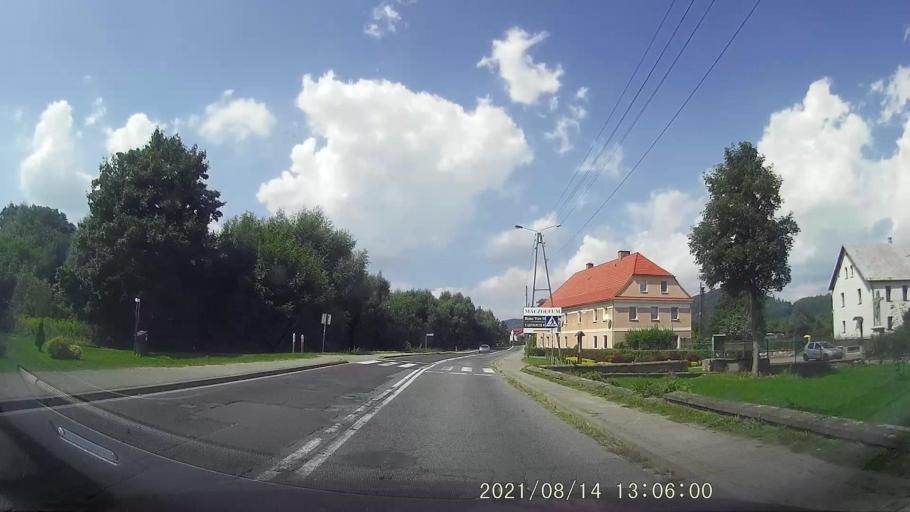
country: PL
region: Lower Silesian Voivodeship
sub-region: Powiat klodzki
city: Klodzko
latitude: 50.3599
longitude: 16.7209
